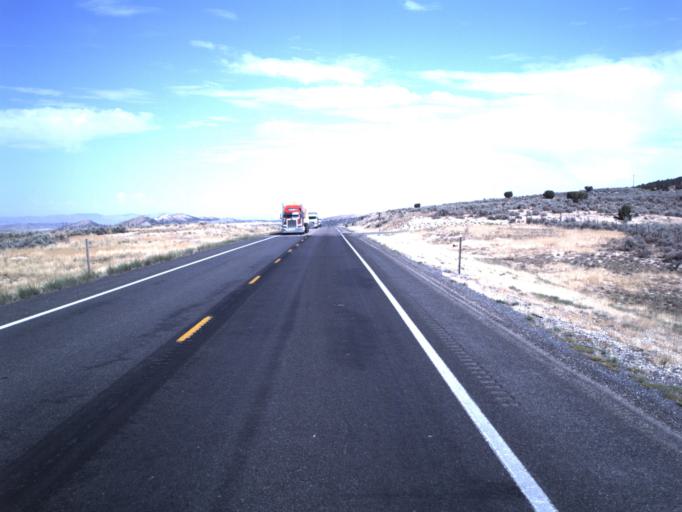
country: US
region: Utah
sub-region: Sanpete County
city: Gunnison
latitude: 39.3202
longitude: -111.9070
